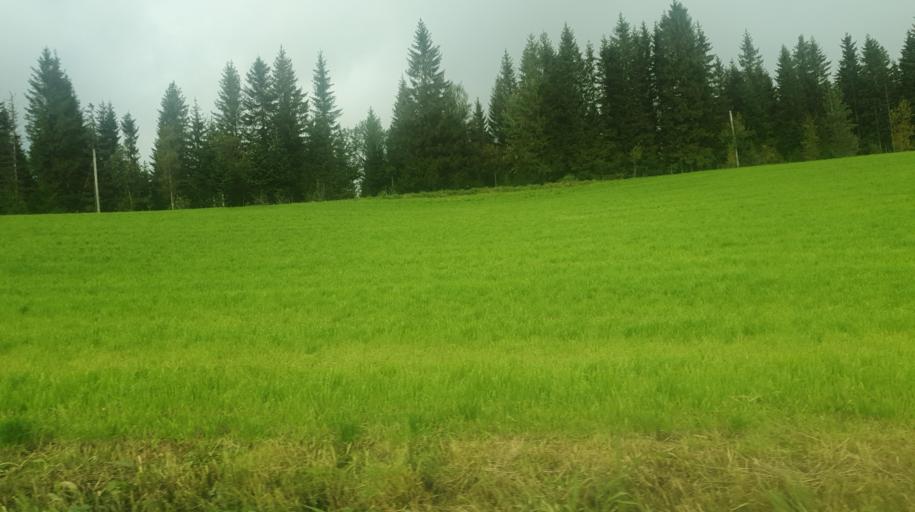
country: NO
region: Nord-Trondelag
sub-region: Levanger
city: Skogn
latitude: 63.6185
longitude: 11.1948
